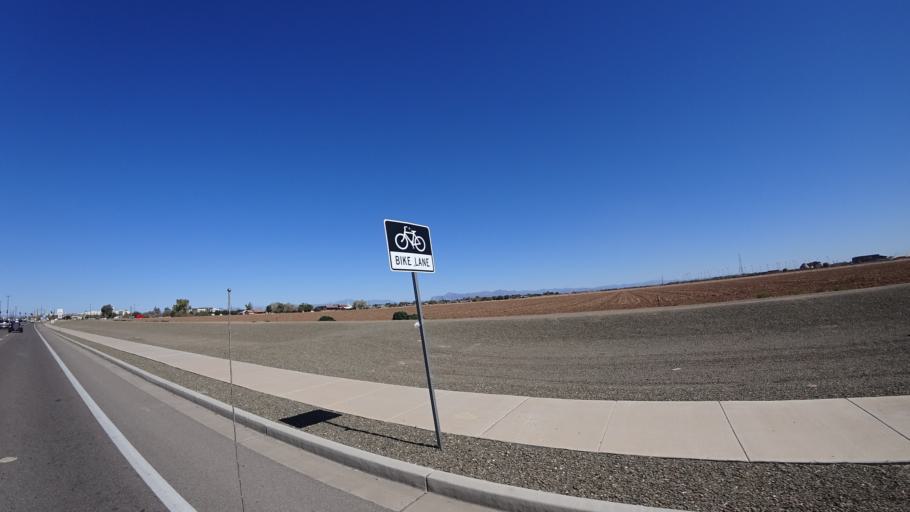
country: US
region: Arizona
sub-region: Maricopa County
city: Gilbert
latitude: 33.2743
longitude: -111.7552
